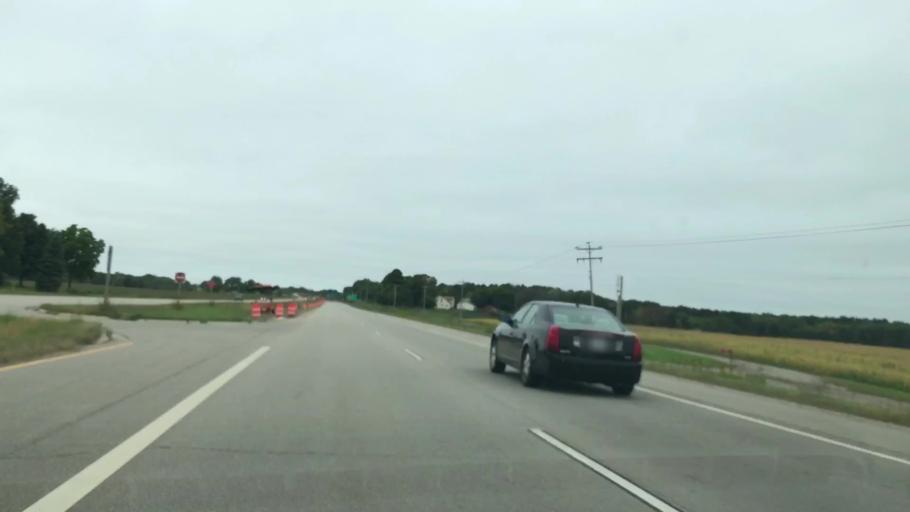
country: US
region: Wisconsin
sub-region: Oconto County
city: Oconto Falls
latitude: 44.7975
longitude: -88.0267
